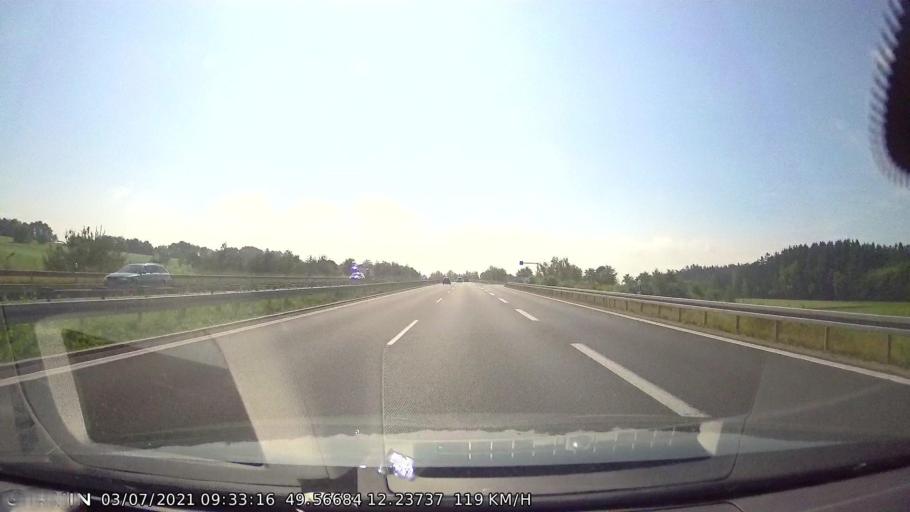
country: DE
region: Bavaria
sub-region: Upper Palatinate
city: Leuchtenberg
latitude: 49.5665
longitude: 12.2373
